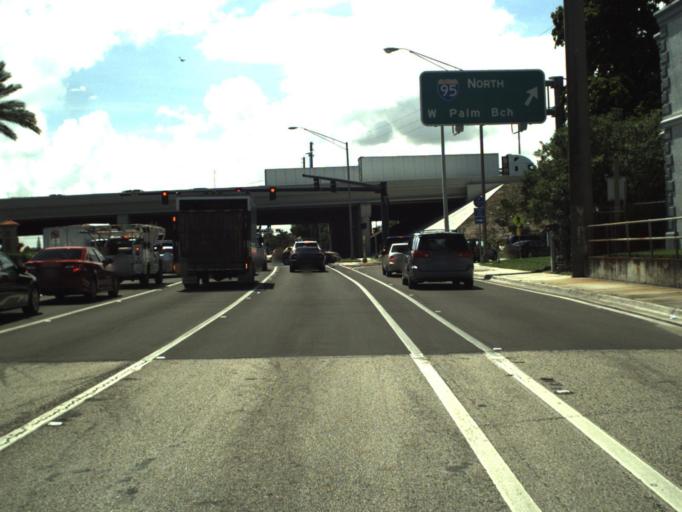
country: US
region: Florida
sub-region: Broward County
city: Pembroke Park
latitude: 25.9963
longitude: -80.1647
